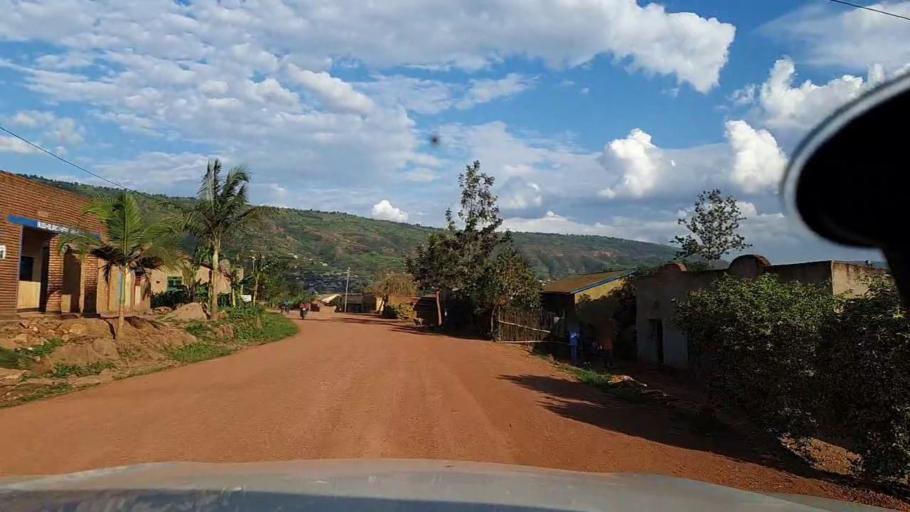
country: RW
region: Kigali
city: Kigali
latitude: -1.9031
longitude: 29.9656
